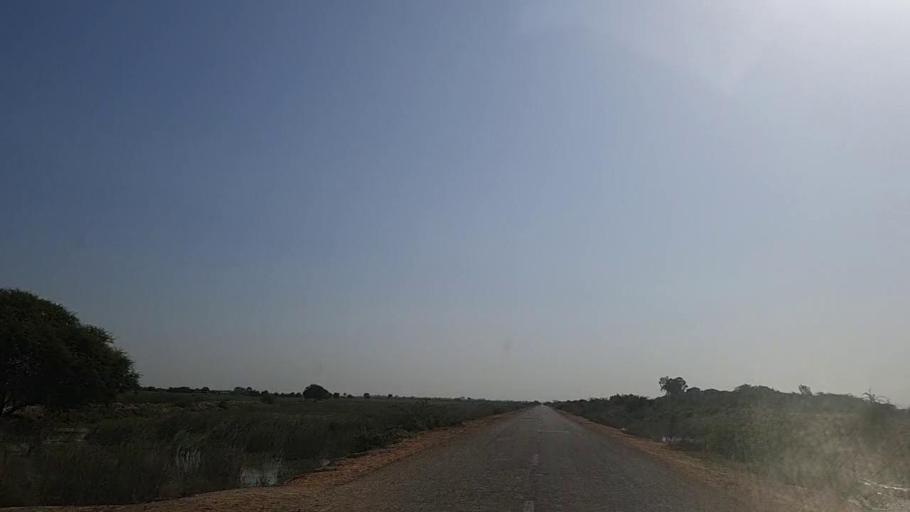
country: PK
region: Sindh
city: Jati
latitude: 24.4514
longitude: 68.2637
